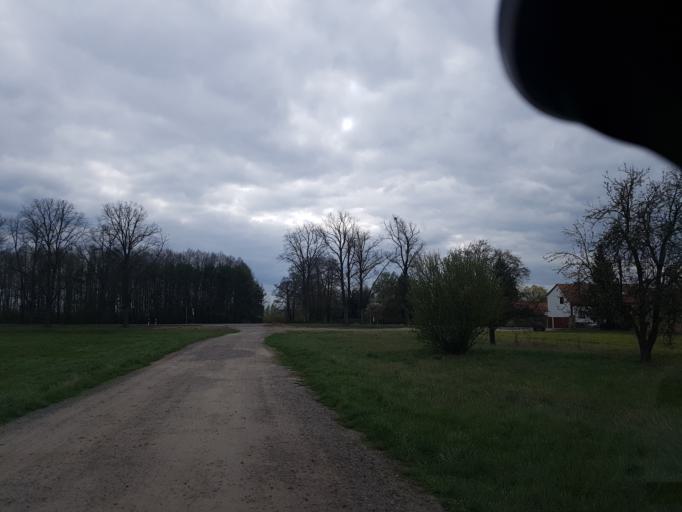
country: DE
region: Brandenburg
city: Bruck
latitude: 52.2001
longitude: 12.7768
